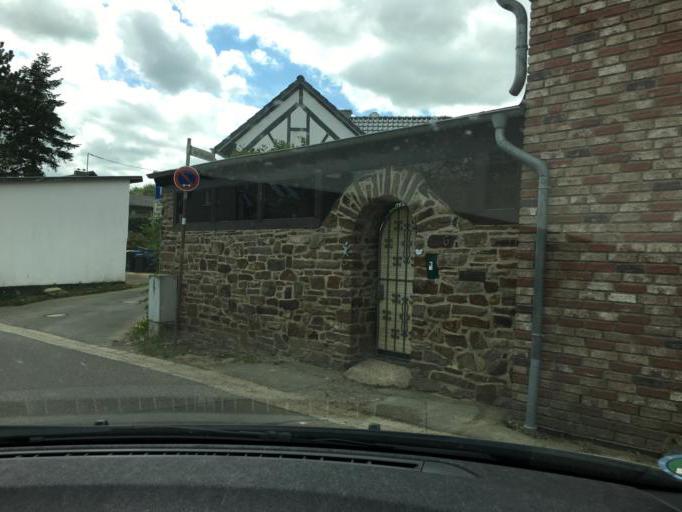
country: DE
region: Rheinland-Pfalz
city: Kirchsahr
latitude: 50.5153
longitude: 6.8726
